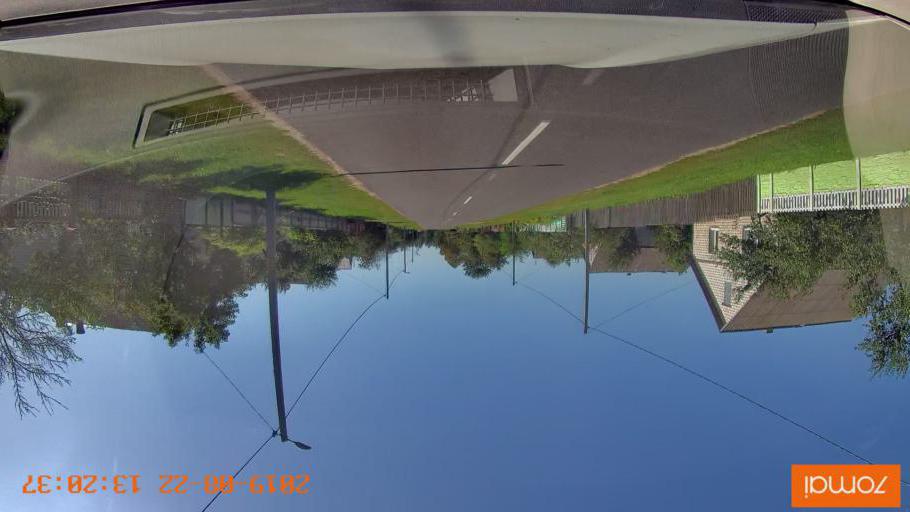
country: BY
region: Minsk
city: Urechcha
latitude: 53.2289
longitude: 27.9703
